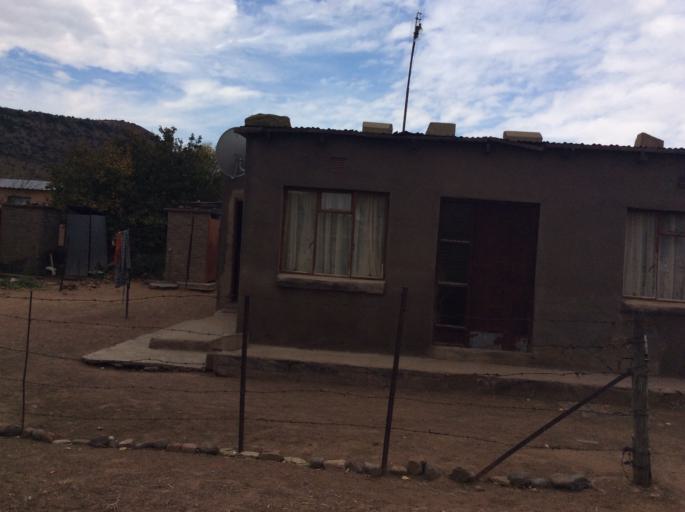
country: LS
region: Mafeteng
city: Mafeteng
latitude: -29.7196
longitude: 27.0311
